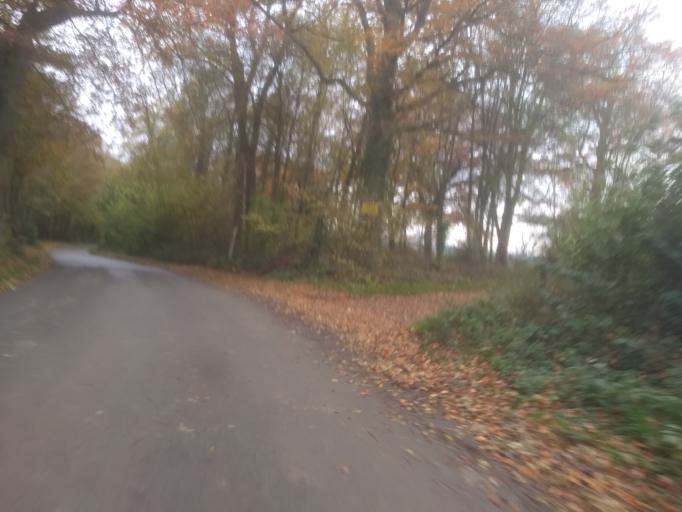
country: FR
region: Nord-Pas-de-Calais
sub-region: Departement du Pas-de-Calais
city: Dainville
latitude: 50.2581
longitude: 2.7183
